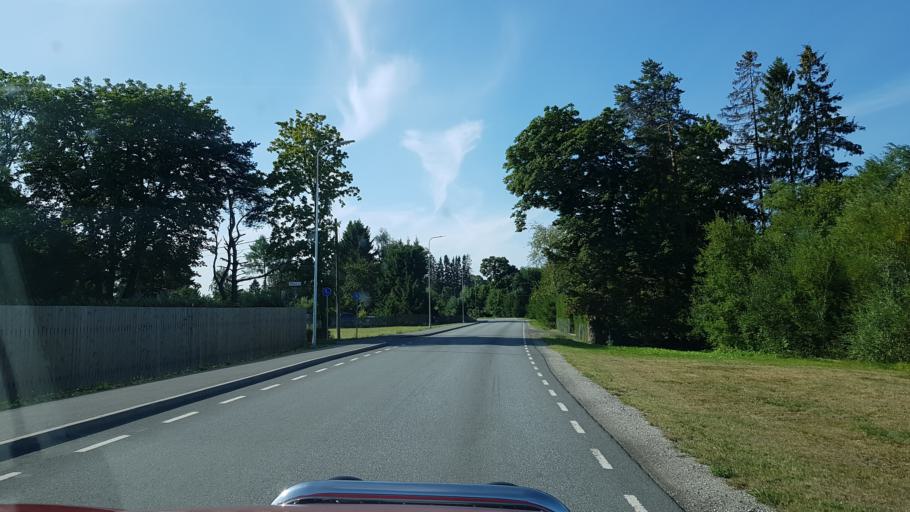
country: EE
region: Harju
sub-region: Joelaehtme vald
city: Loo
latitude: 59.3941
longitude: 24.9343
